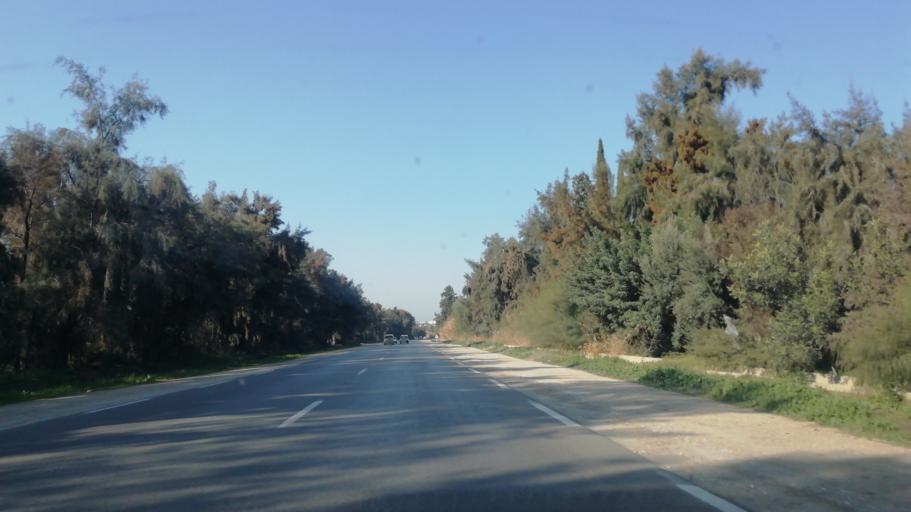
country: DZ
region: Relizane
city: Relizane
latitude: 35.7230
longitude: 0.4904
